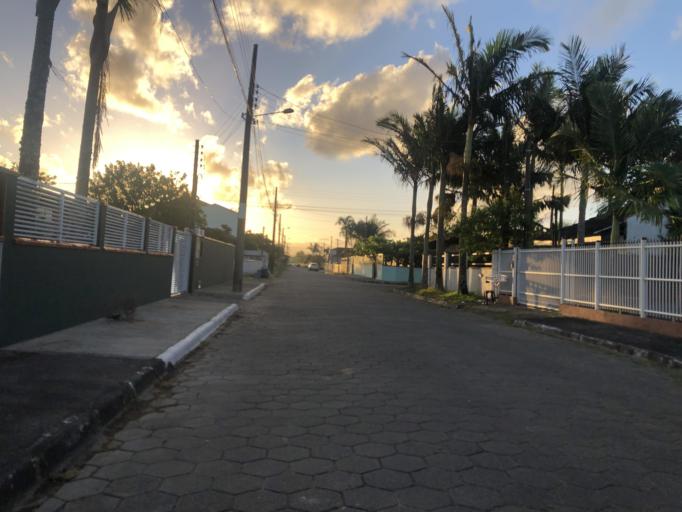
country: BR
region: Santa Catarina
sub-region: Sao Francisco Do Sul
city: Sao Francisco do Sul
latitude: -26.2194
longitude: -48.5258
